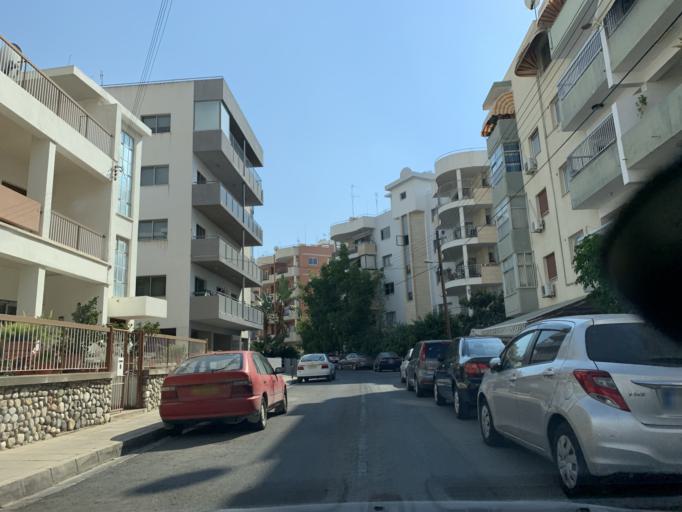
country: CY
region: Lefkosia
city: Nicosia
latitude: 35.1538
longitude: 33.3612
